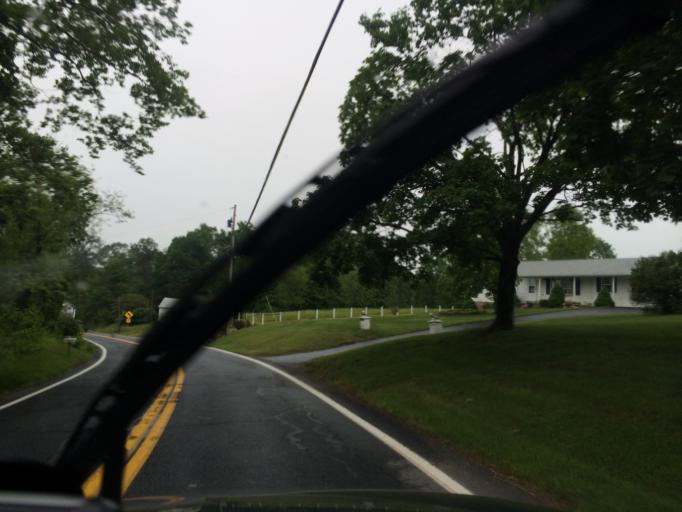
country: US
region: Maryland
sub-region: Frederick County
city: Thurmont
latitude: 39.6102
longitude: -77.3351
